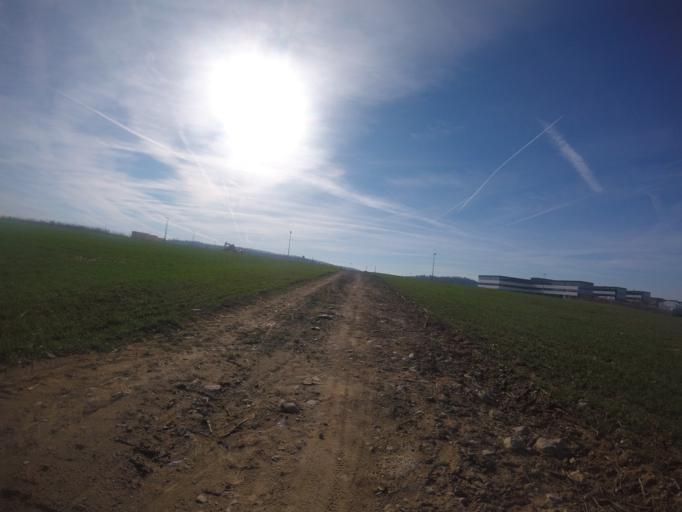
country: DE
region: Baden-Wuerttemberg
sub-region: Regierungsbezirk Stuttgart
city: Abstatt
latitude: 49.0818
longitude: 9.3058
